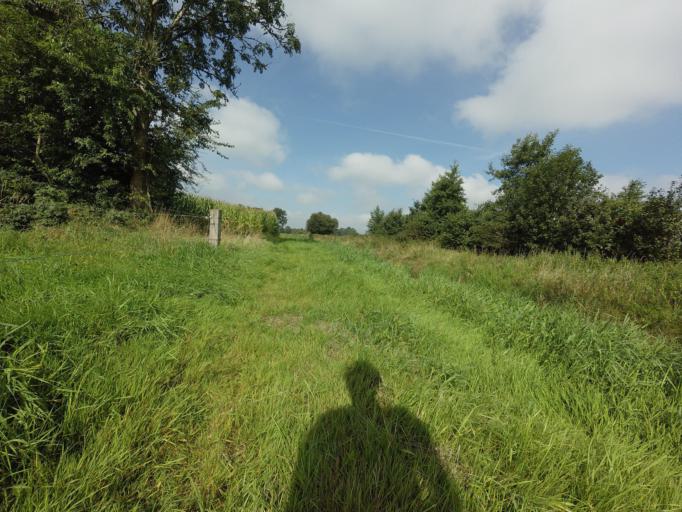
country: NL
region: Drenthe
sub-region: Gemeente Tynaarlo
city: Vries
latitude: 53.1113
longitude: 6.5504
